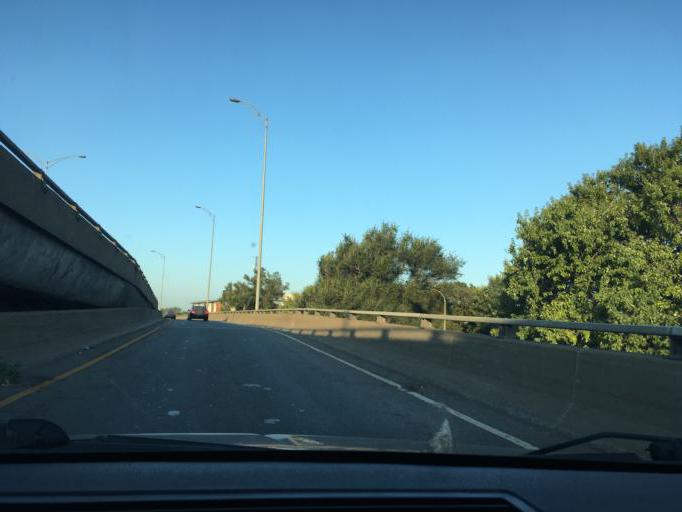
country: CA
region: Quebec
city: Mont-Royal
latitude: 45.5502
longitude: -73.6323
